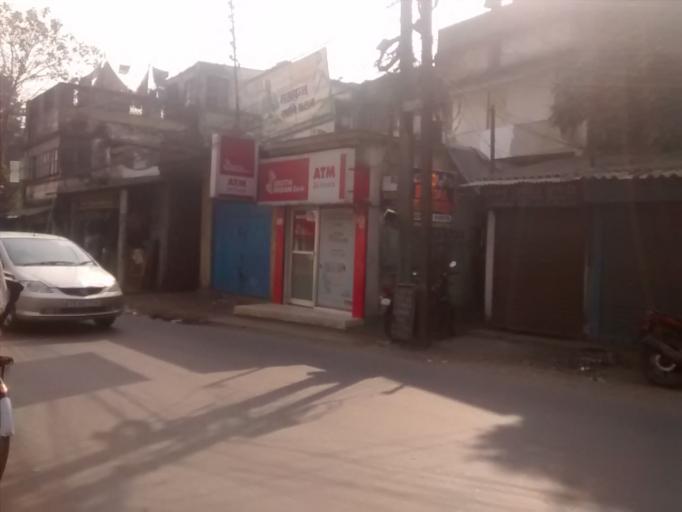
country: IN
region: West Bengal
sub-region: South 24 Paraganas
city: Baruipur
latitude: 22.4490
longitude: 88.3912
